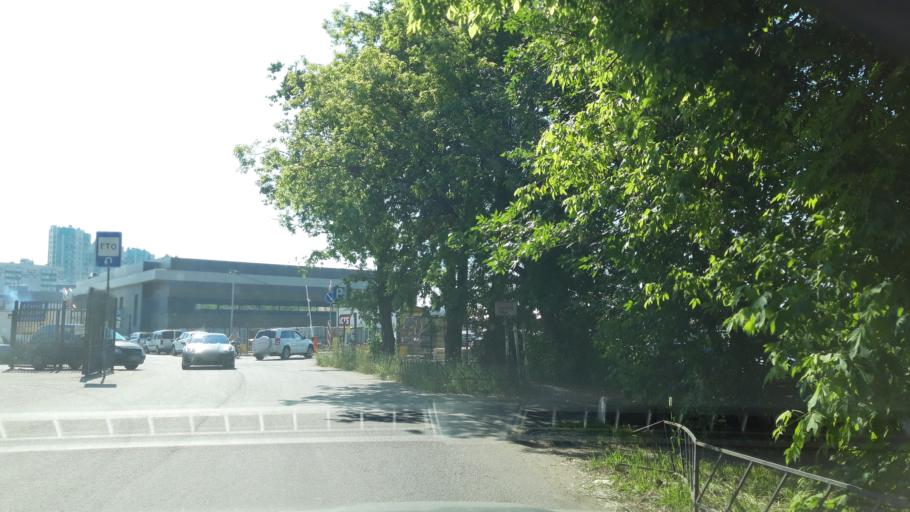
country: RU
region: Moscow
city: Zelenograd
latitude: 55.9829
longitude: 37.1715
